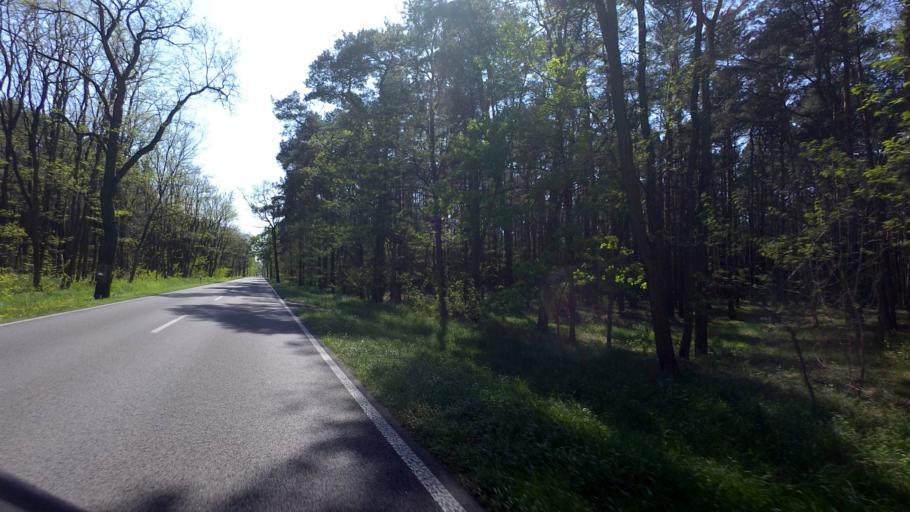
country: DE
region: Brandenburg
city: Tauche
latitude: 52.1050
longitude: 14.1832
